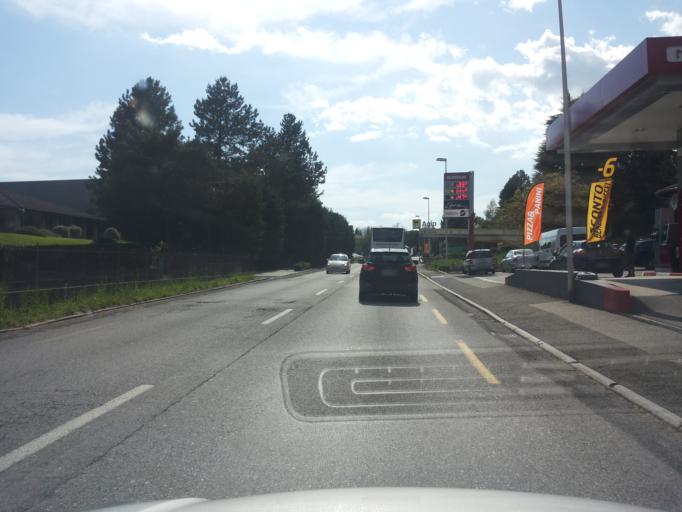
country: CH
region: Ticino
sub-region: Mendrisio District
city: Stabio
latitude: 45.8458
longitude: 8.9308
